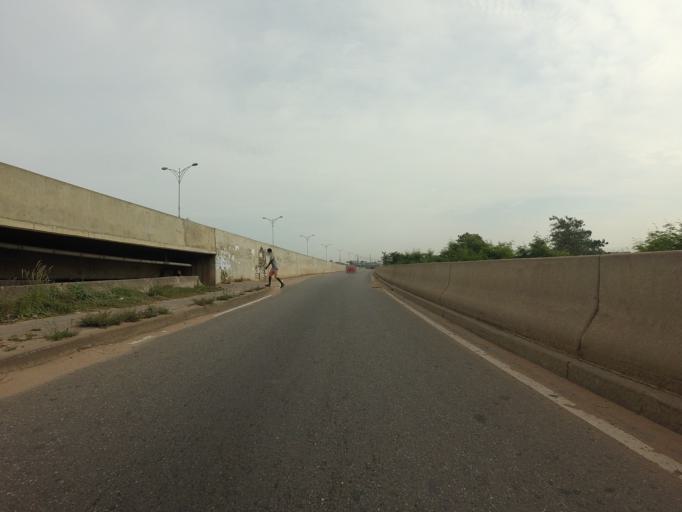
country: GH
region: Greater Accra
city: Gbawe
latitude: 5.5739
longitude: -0.2826
